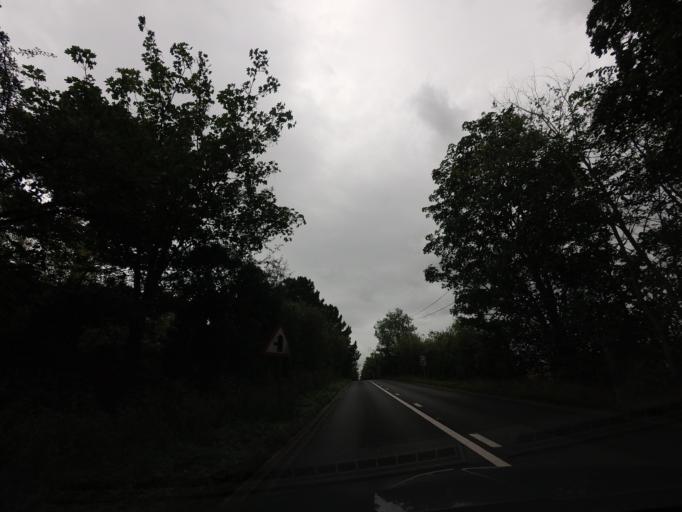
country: GB
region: England
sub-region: Kent
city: East Peckham
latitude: 51.2378
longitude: 0.3805
